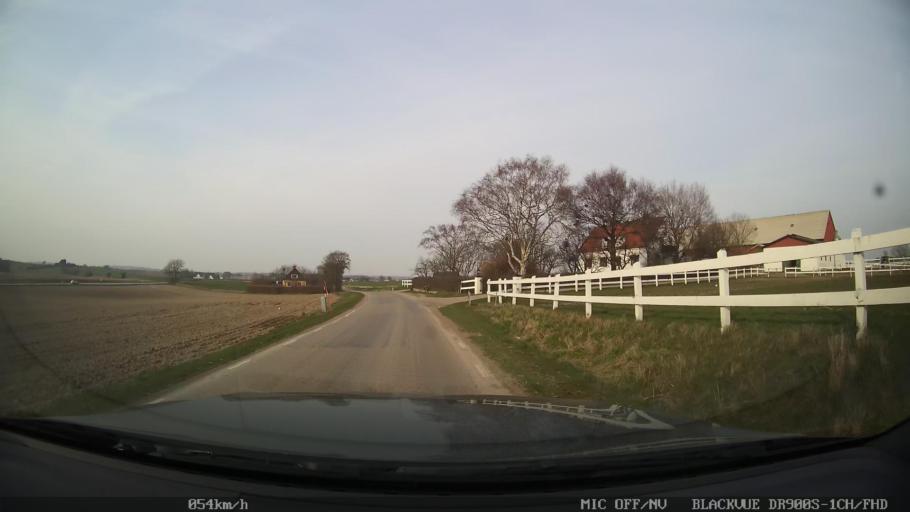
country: SE
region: Skane
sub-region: Ystads Kommun
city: Ystad
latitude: 55.4724
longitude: 13.8004
